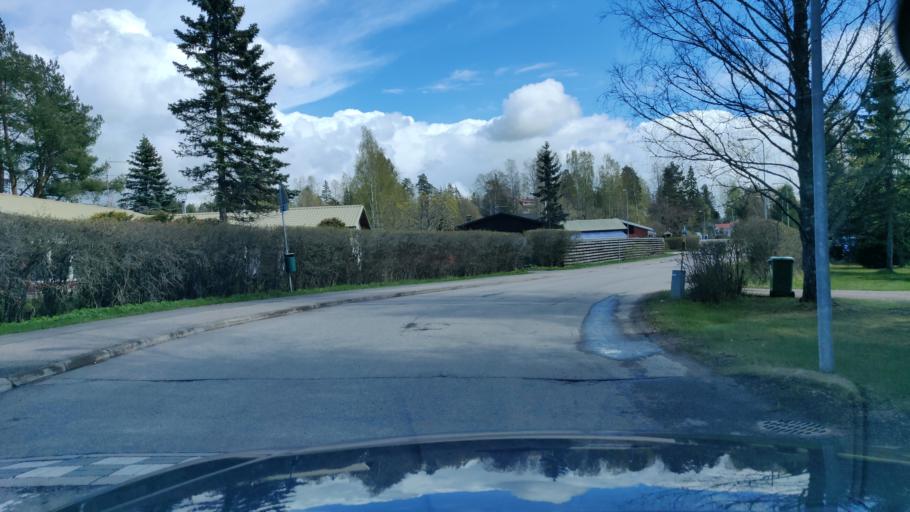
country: FI
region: Uusimaa
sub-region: Helsinki
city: Nurmijaervi
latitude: 60.3653
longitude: 24.7440
